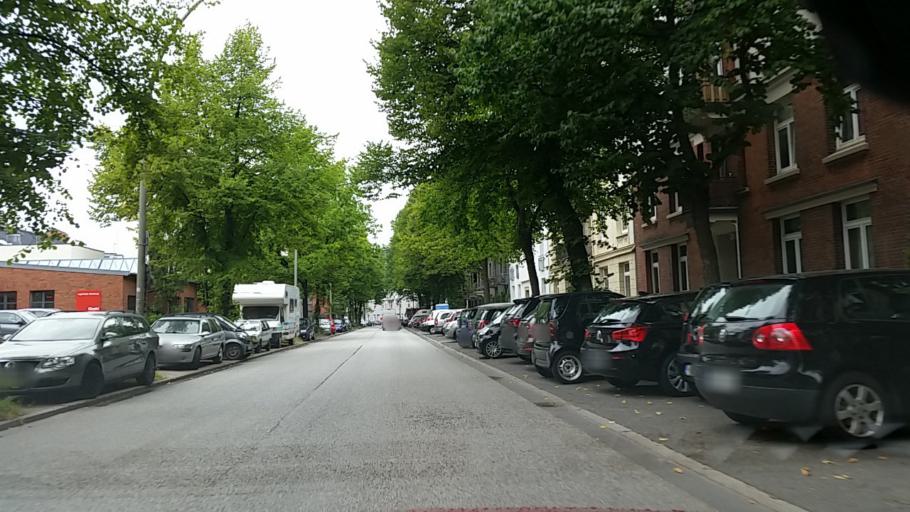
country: DE
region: Hamburg
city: Altona
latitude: 53.5616
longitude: 9.9201
